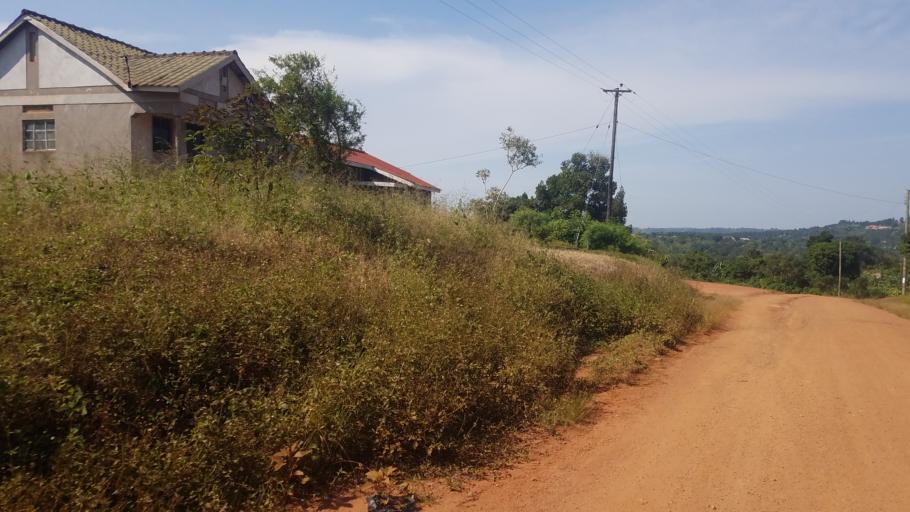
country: UG
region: Central Region
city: Masaka
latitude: -0.3069
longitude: 31.6830
